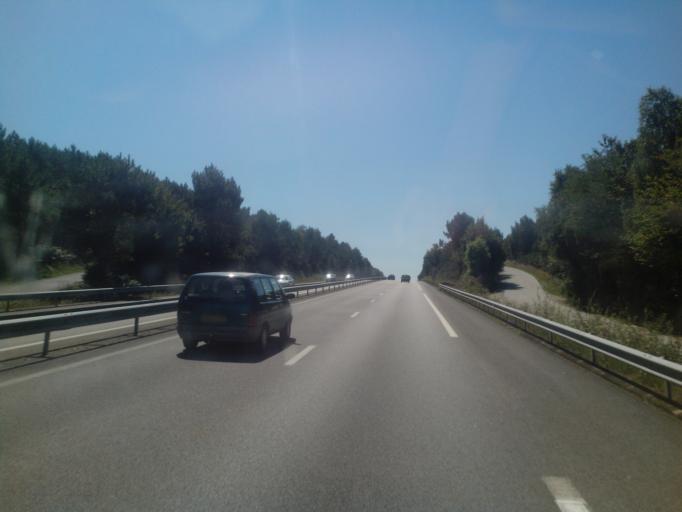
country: FR
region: Brittany
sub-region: Departement du Morbihan
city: Malestroit
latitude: 47.8179
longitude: -2.4366
